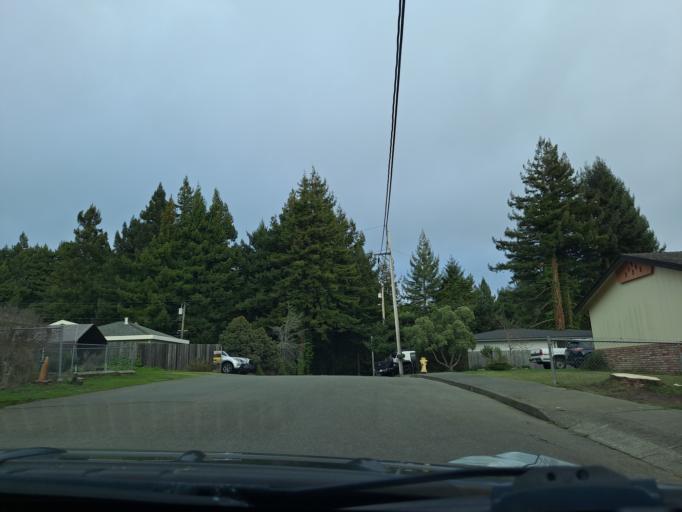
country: US
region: California
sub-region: Humboldt County
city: Fortuna
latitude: 40.6038
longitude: -124.1552
